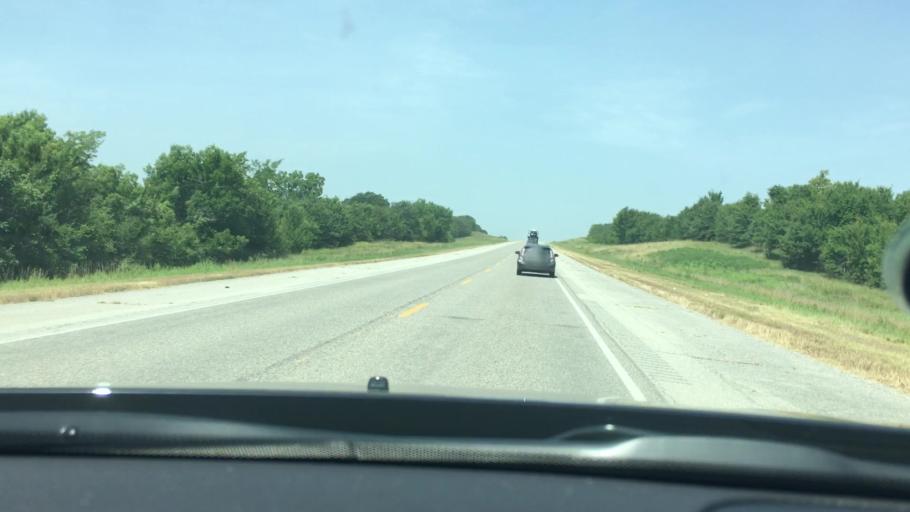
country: US
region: Oklahoma
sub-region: Coal County
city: Coalgate
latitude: 34.6110
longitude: -96.3998
